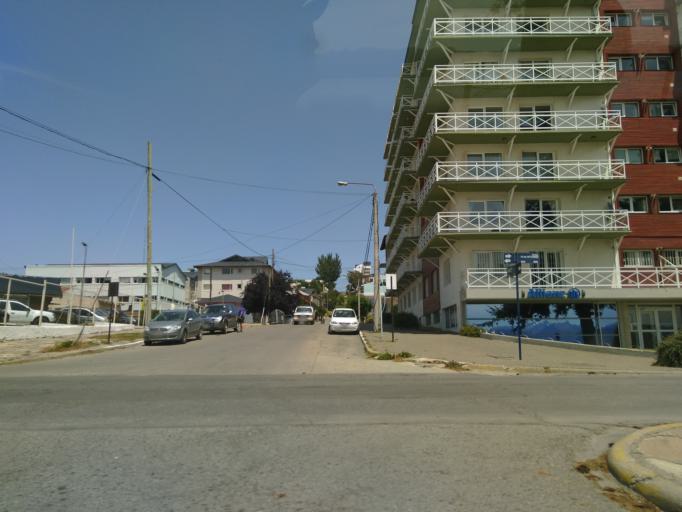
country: AR
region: Rio Negro
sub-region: Departamento de Bariloche
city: San Carlos de Bariloche
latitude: -41.1327
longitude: -71.2967
